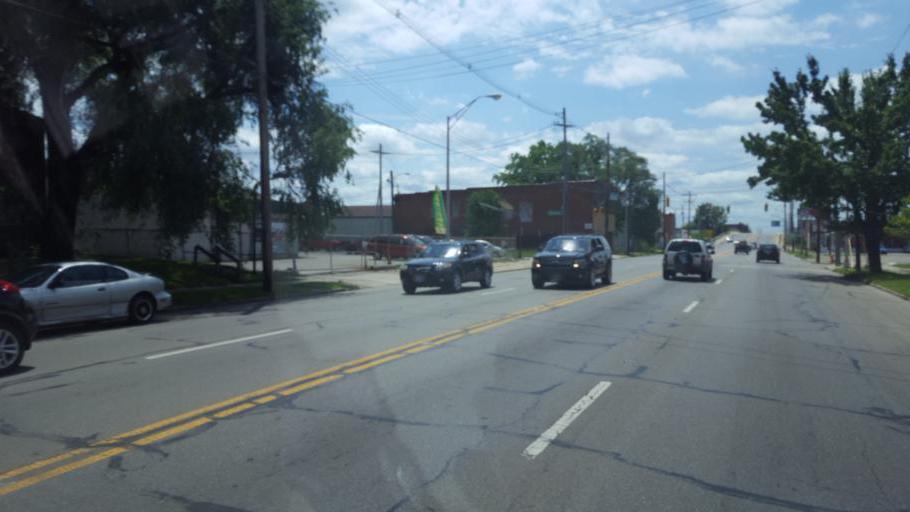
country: US
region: Ohio
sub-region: Franklin County
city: Columbus
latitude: 39.9248
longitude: -82.9956
